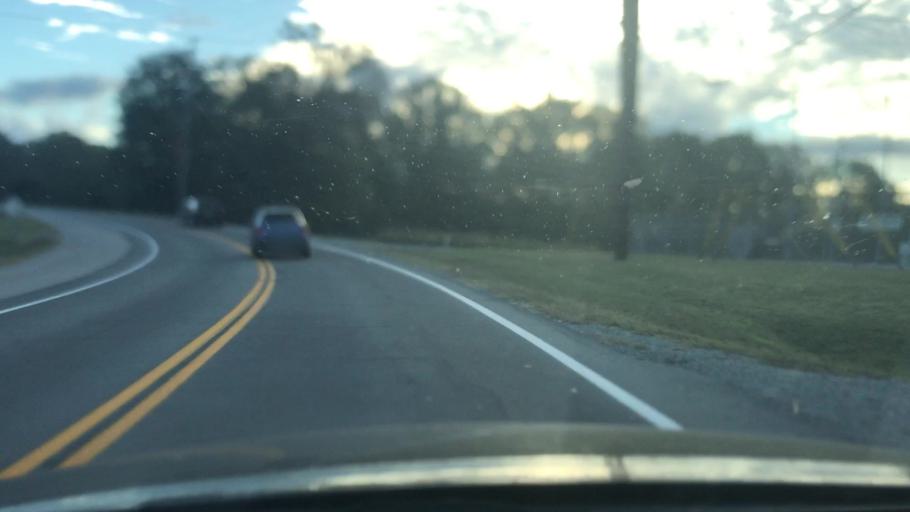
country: US
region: Tennessee
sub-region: Cheatham County
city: Ashland City
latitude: 36.2628
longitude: -87.0641
